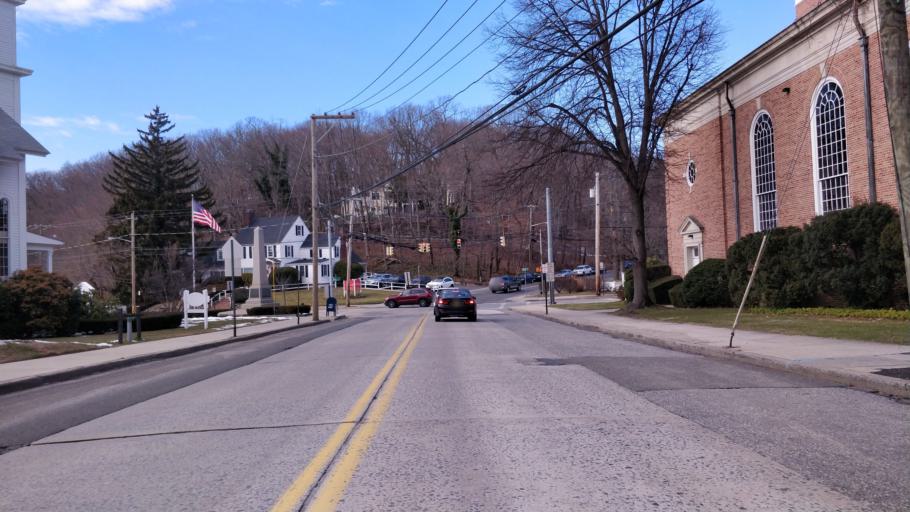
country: US
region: New York
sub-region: Suffolk County
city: Northport
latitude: 40.9008
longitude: -73.3425
